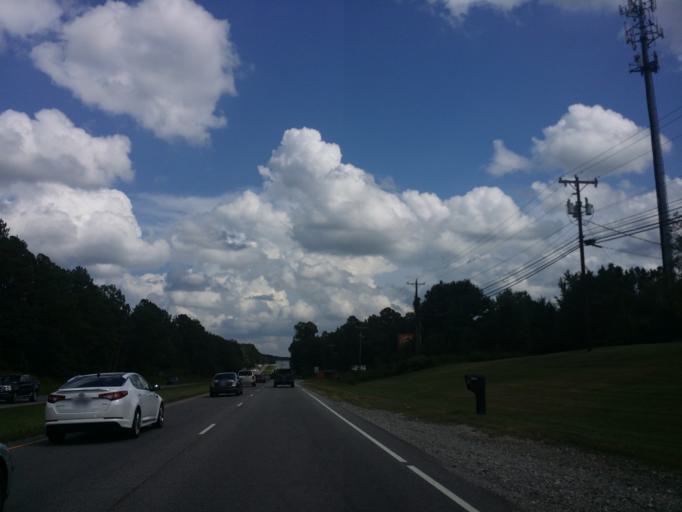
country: US
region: North Carolina
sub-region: Durham County
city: Durham
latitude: 35.9473
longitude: -78.8345
